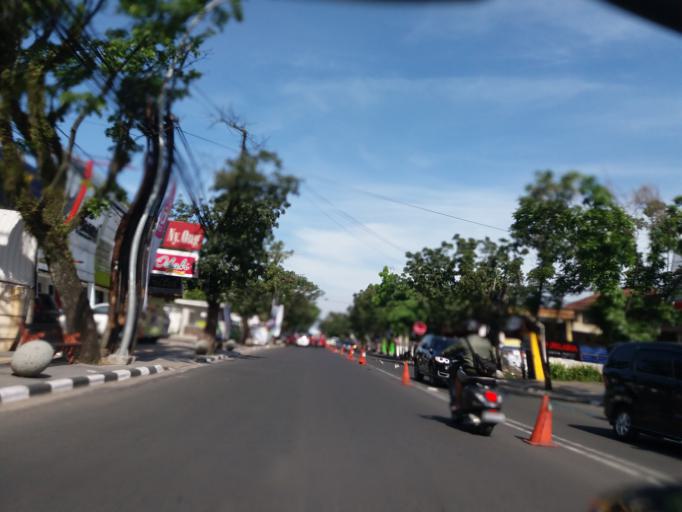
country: ID
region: West Java
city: Bandung
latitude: -6.9383
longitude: 107.6240
